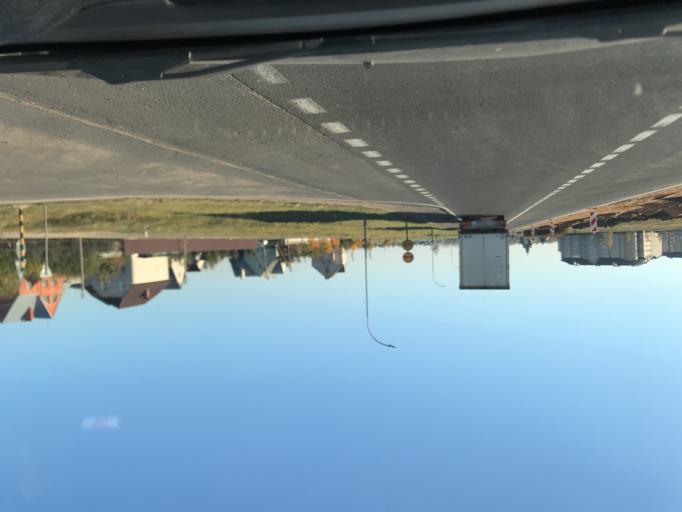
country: BY
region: Minsk
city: Slutsk
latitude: 53.0453
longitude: 27.5728
